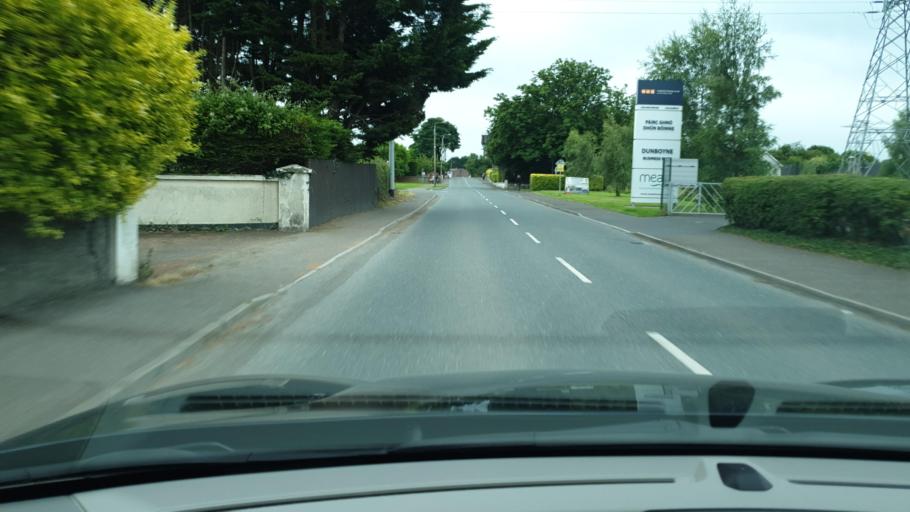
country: IE
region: Leinster
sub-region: An Mhi
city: Dunboyne
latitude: 53.4246
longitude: -6.4722
